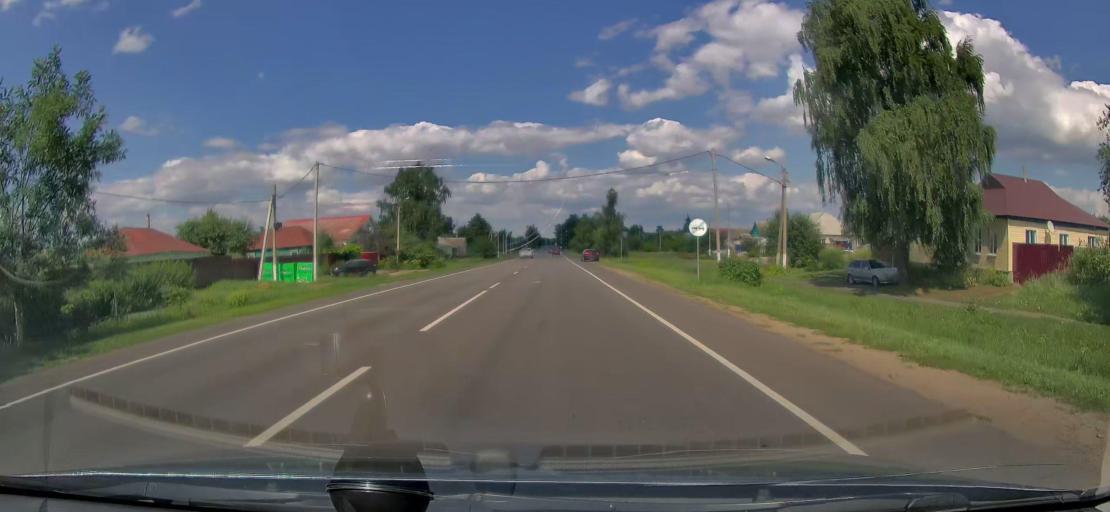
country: RU
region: Kursk
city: Zolotukhino
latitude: 51.9157
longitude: 36.3060
